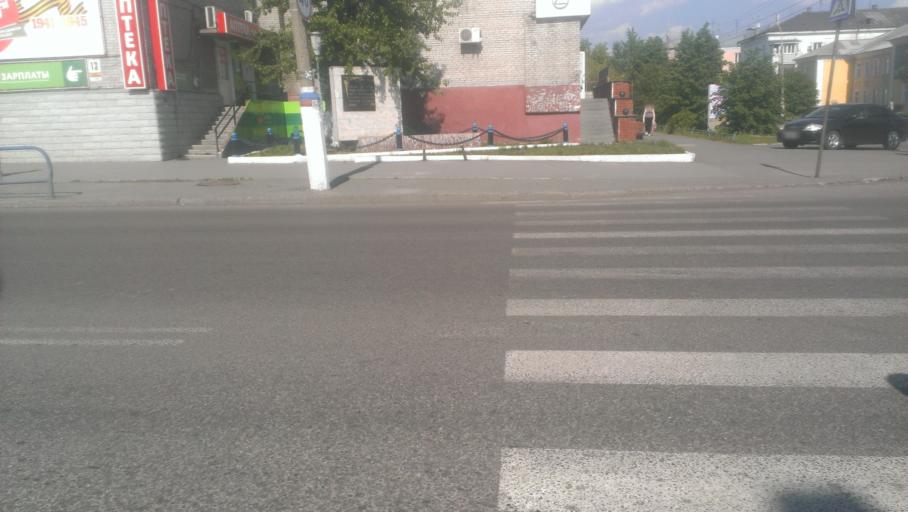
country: RU
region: Altai Krai
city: Novoaltaysk
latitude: 53.3919
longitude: 83.9343
